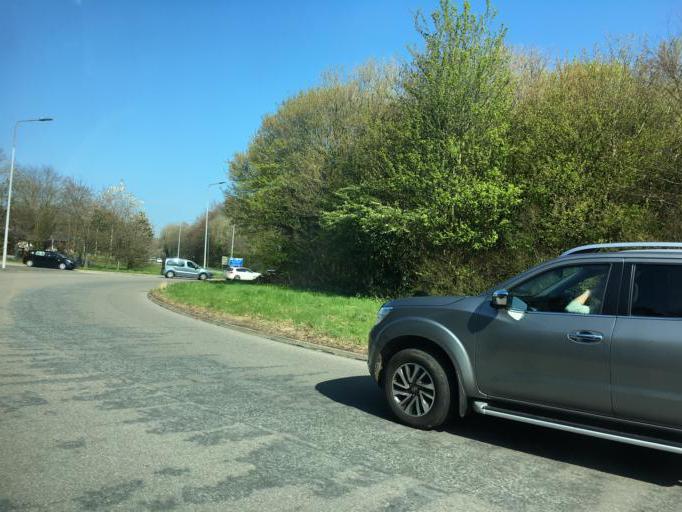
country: GB
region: Wales
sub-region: Gwynedd
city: Y Felinheli
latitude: 53.1962
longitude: -4.1831
